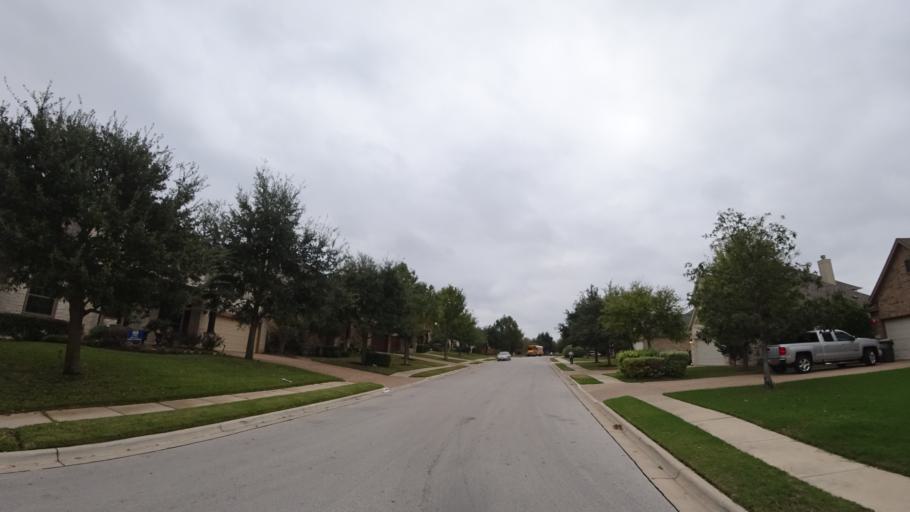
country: US
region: Texas
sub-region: Travis County
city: Hudson Bend
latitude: 30.3635
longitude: -97.9098
